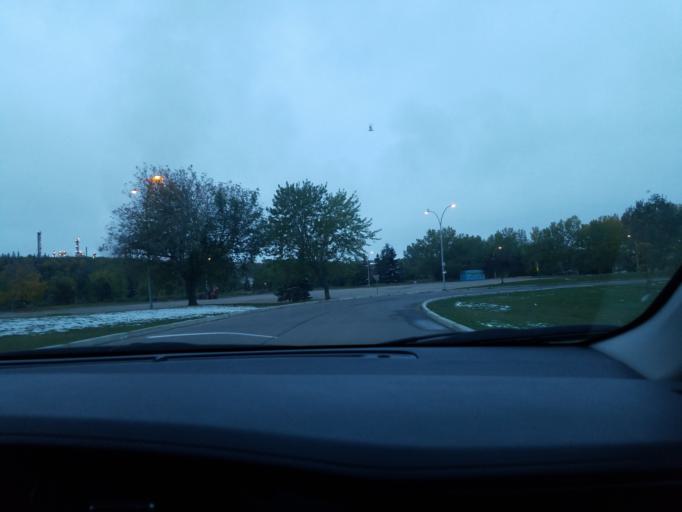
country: CA
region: Alberta
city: Edmonton
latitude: 53.5553
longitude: -113.3893
